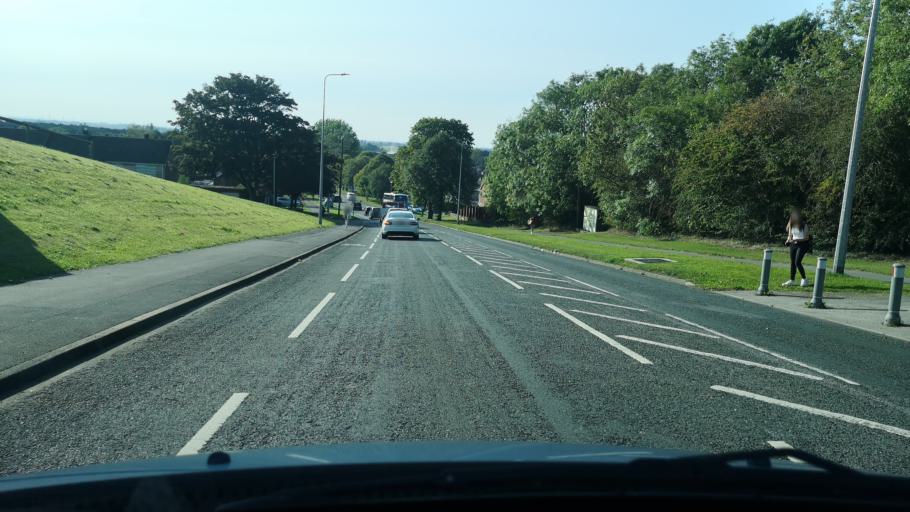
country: GB
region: England
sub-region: North Lincolnshire
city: Scunthorpe
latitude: 53.5744
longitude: -0.6715
